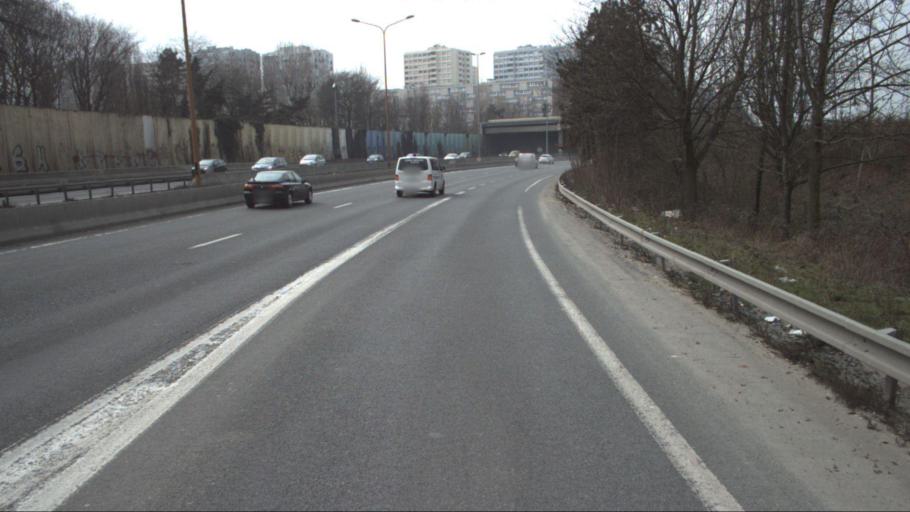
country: FR
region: Ile-de-France
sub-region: Departement des Hauts-de-Seine
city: Bois-Colombes
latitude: 48.9339
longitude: 2.2766
